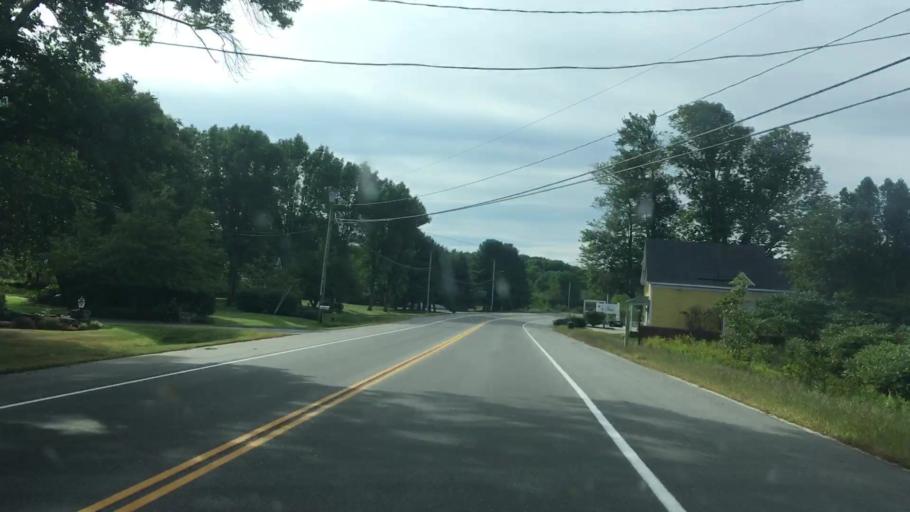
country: US
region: Maine
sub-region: Cumberland County
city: Cumberland Center
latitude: 43.7560
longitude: -70.3007
